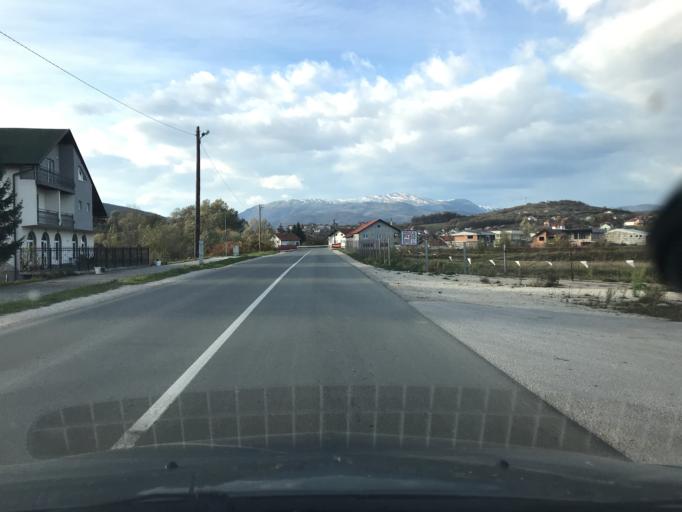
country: BA
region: Federation of Bosnia and Herzegovina
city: Vitez
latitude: 44.1665
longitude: 17.7701
